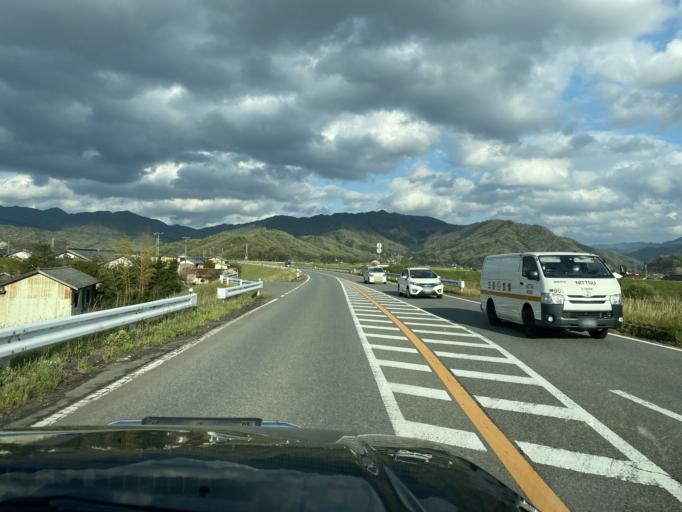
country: JP
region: Hyogo
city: Toyooka
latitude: 35.4890
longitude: 134.8494
